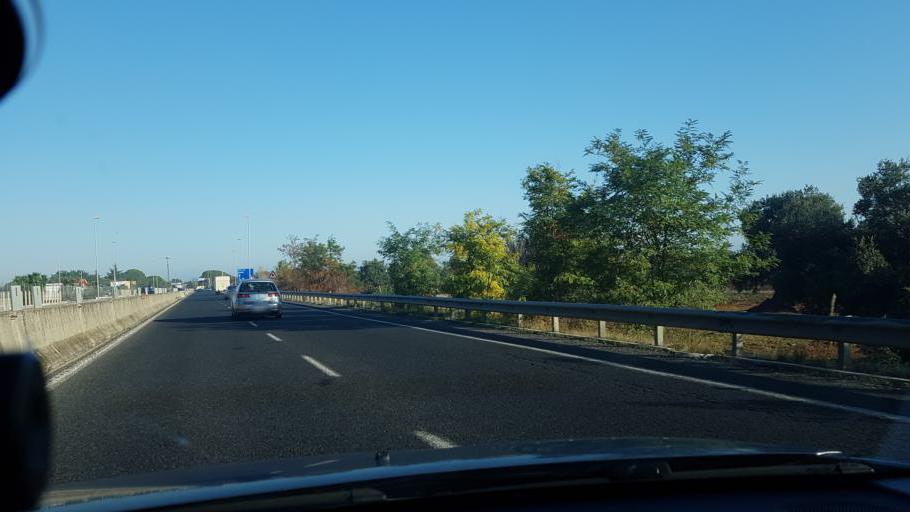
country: IT
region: Apulia
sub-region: Provincia di Bari
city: Monopoli
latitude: 40.9151
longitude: 17.3201
